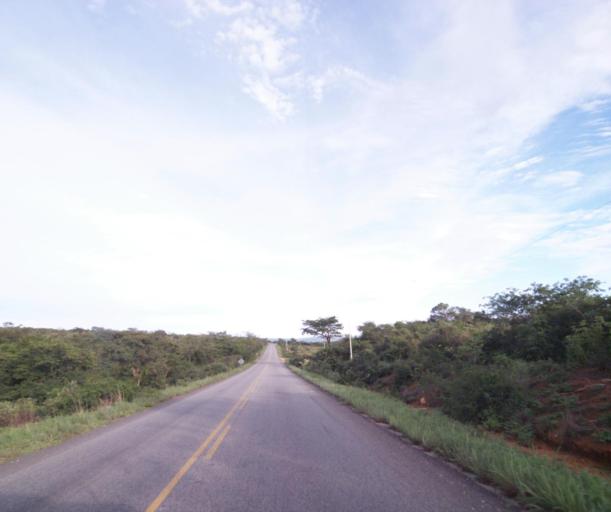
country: BR
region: Bahia
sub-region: Caetite
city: Caetite
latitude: -14.1714
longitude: -42.2956
